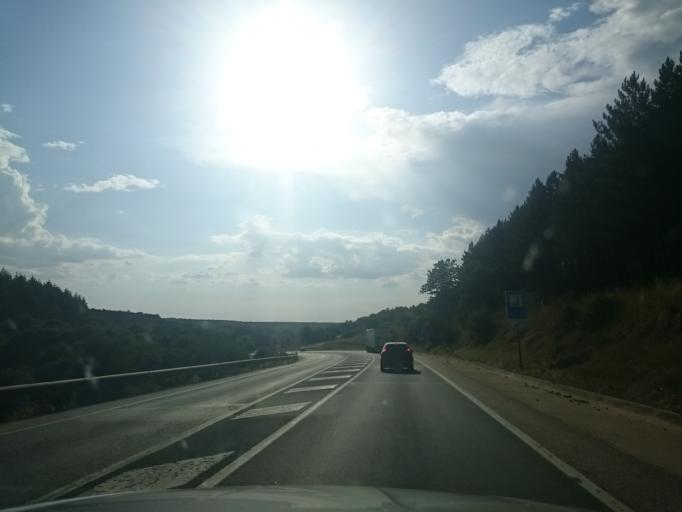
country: ES
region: Castille and Leon
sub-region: Provincia de Burgos
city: Cerraton de Juarros
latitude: 42.3640
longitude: -3.3661
